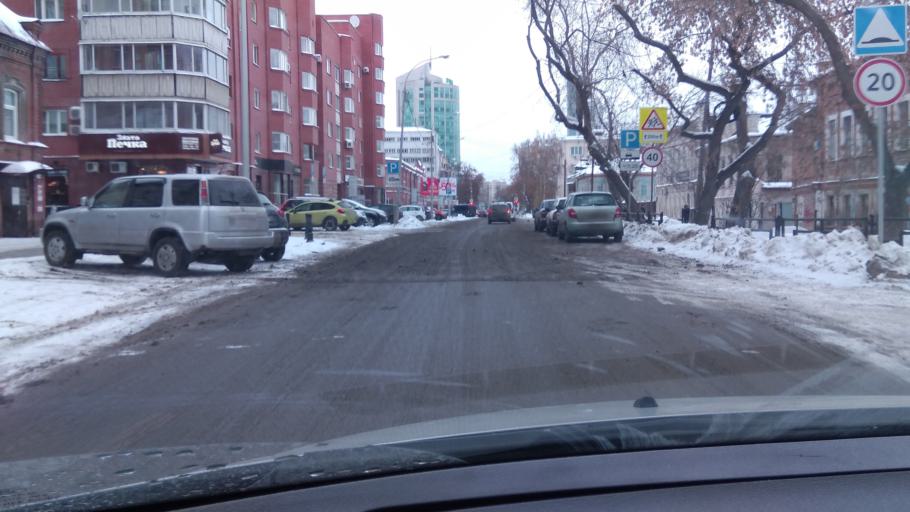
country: RU
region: Sverdlovsk
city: Yekaterinburg
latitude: 56.8313
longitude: 60.5932
